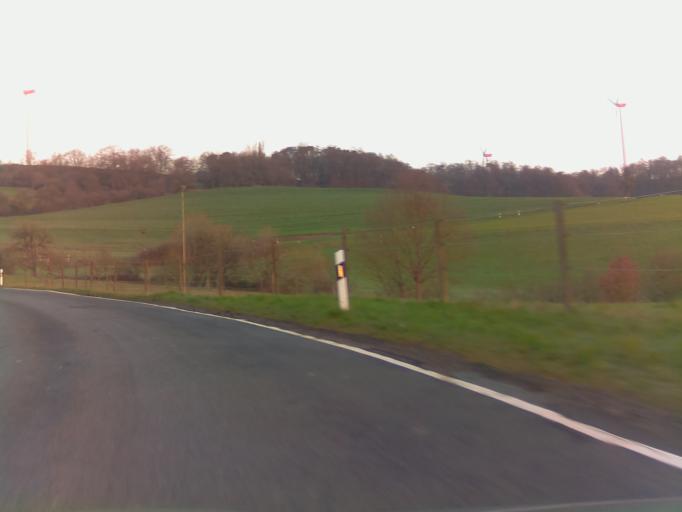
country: DE
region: Rheinland-Pfalz
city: Kirrweiler
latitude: 49.6400
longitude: 7.5054
